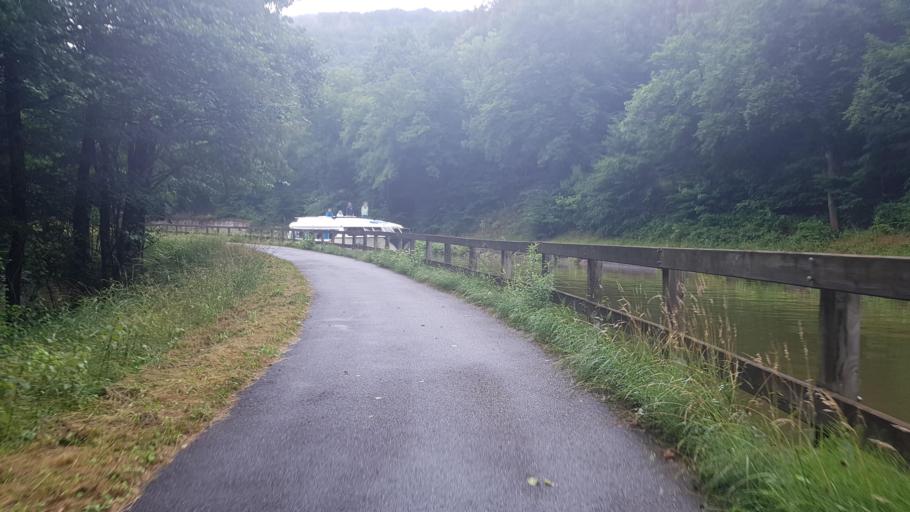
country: FR
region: Lorraine
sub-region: Departement de la Moselle
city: Phalsbourg
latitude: 48.7285
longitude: 7.2988
